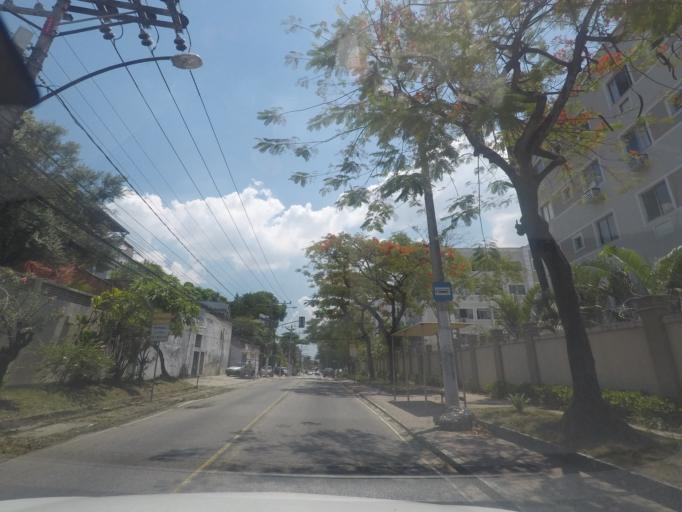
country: BR
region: Rio de Janeiro
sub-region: Duque De Caxias
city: Duque de Caxias
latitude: -22.8186
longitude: -43.3040
